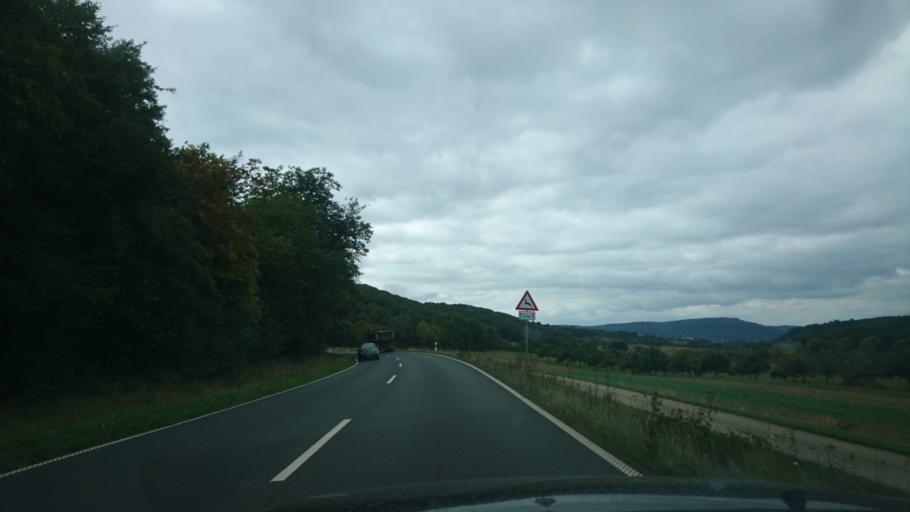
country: DE
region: Rheinland-Pfalz
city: Wiltingen
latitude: 49.6898
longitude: 6.6142
